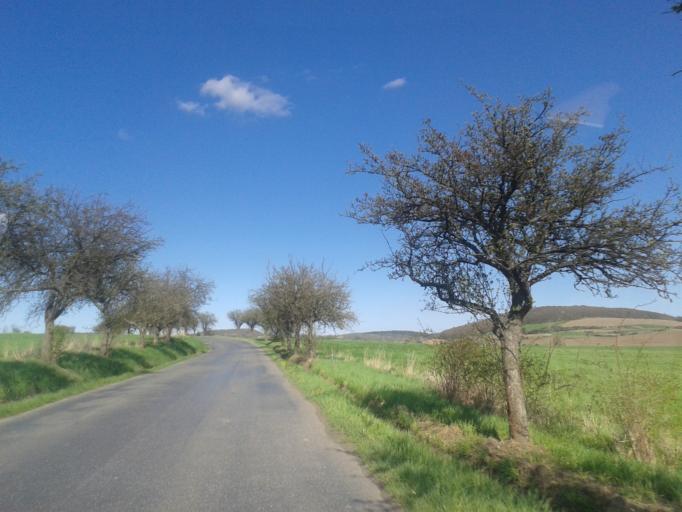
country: CZ
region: Central Bohemia
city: Hostomice
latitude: 49.8874
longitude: 14.0700
